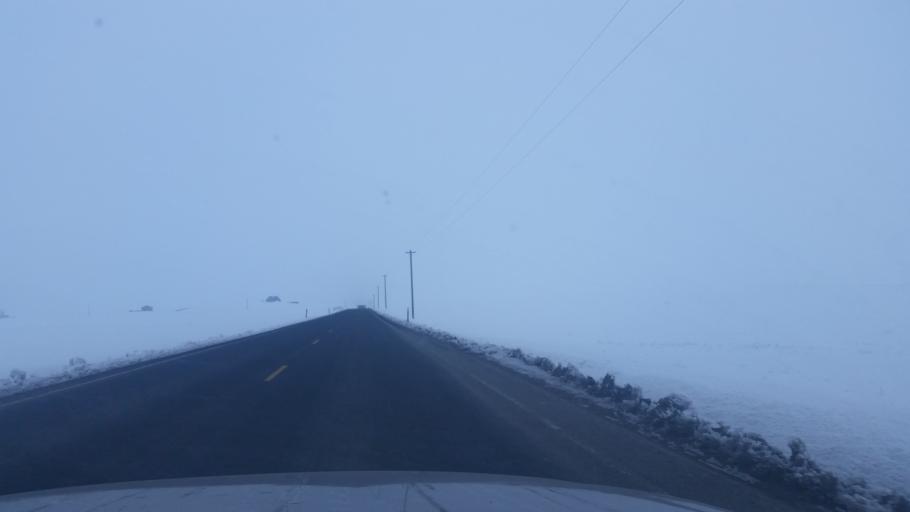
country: US
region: Washington
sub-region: Spokane County
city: Medical Lake
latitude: 47.6581
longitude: -117.8413
